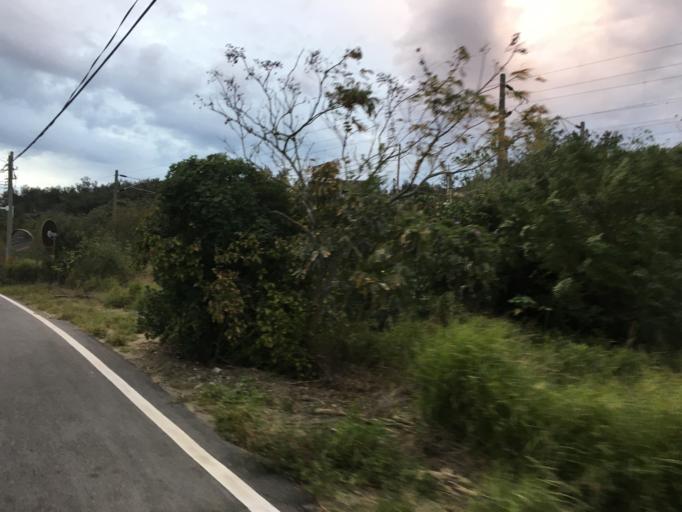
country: TW
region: Taiwan
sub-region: Hsinchu
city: Hsinchu
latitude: 24.7307
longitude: 120.8796
